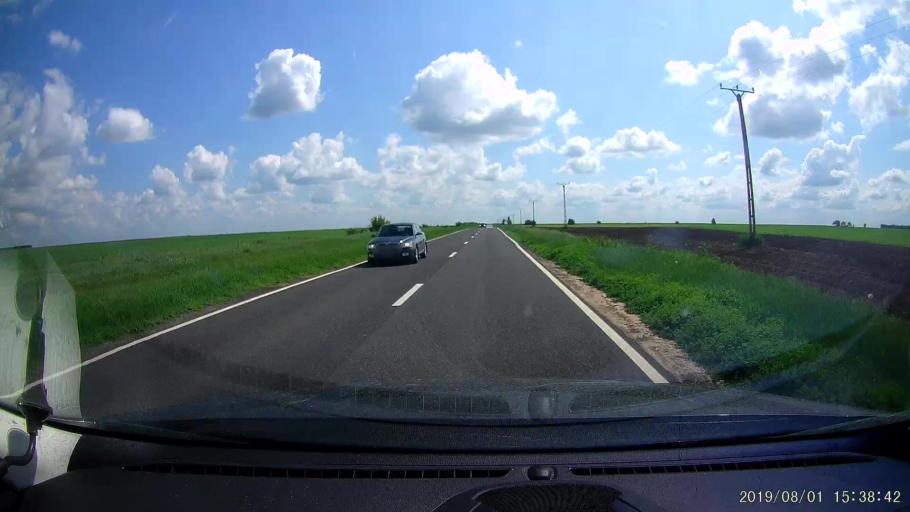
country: RO
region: Braila
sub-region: Comuna Insuratei
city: Insuratei
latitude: 44.8752
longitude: 27.5721
